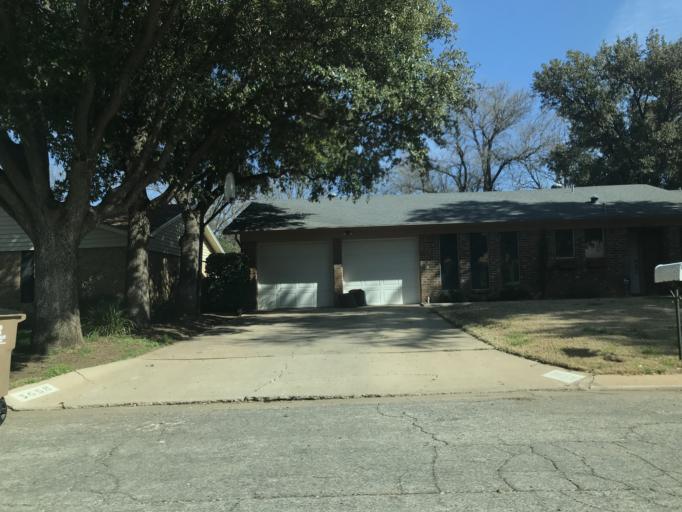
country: US
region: Texas
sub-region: Tom Green County
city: San Angelo
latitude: 31.4342
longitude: -100.4870
